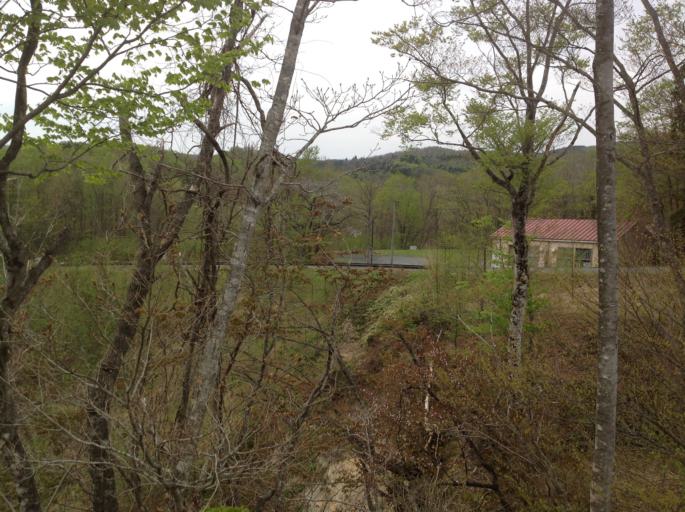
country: JP
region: Iwate
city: Ichinoseki
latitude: 39.0154
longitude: 140.8770
